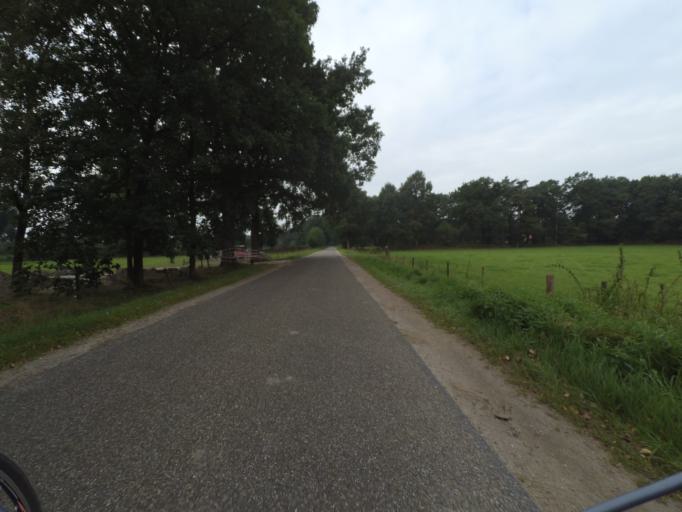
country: NL
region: Overijssel
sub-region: Gemeente Losser
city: Losser
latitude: 52.3342
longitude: 7.0050
